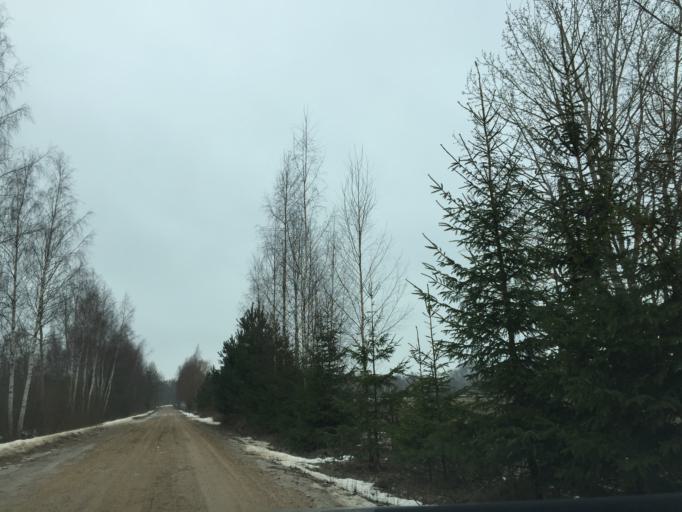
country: LV
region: Lecava
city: Iecava
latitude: 56.5683
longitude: 24.0548
